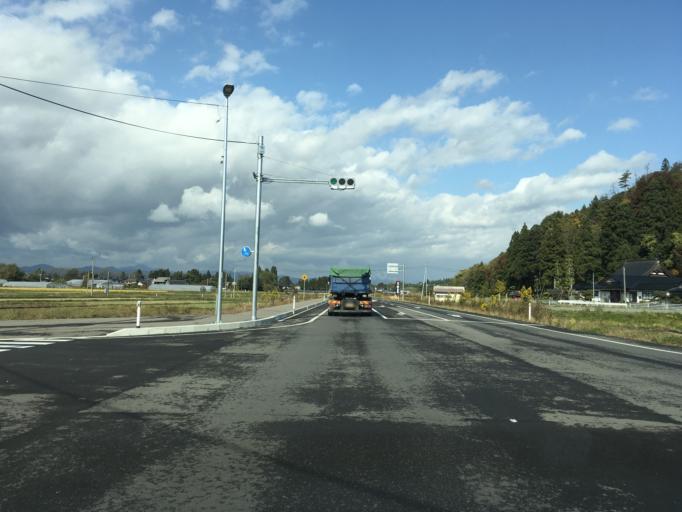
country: JP
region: Iwate
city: Hanamaki
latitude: 39.3667
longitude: 141.1493
